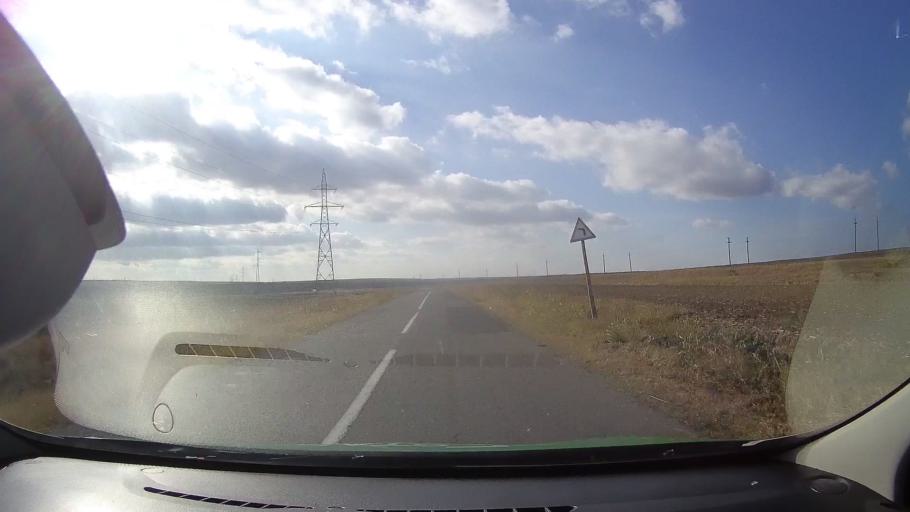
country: RO
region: Constanta
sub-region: Comuna Sacele
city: Sacele
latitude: 44.5039
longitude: 28.6647
